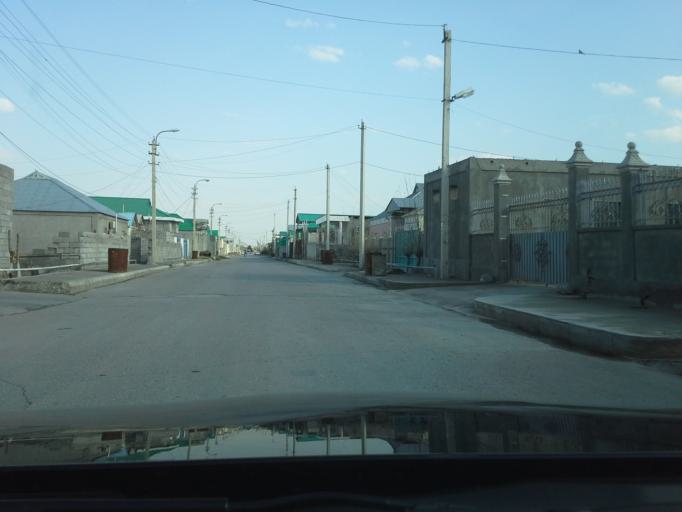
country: TM
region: Ahal
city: Abadan
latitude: 38.0229
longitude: 58.2208
